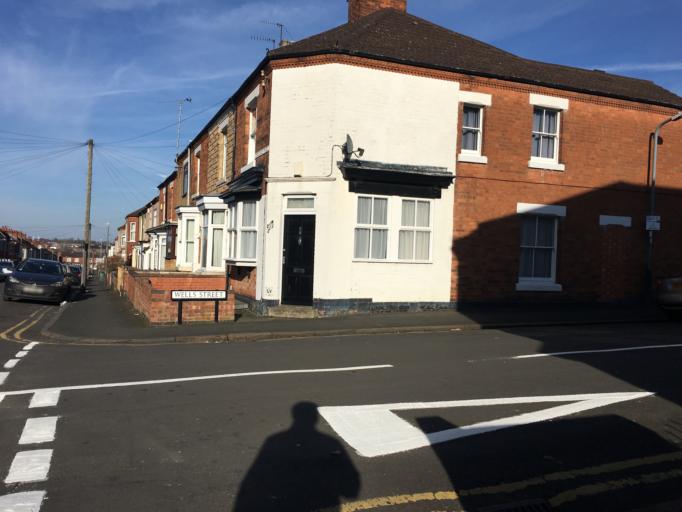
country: GB
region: England
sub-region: Warwickshire
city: Rugby
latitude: 52.3739
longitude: -1.2521
